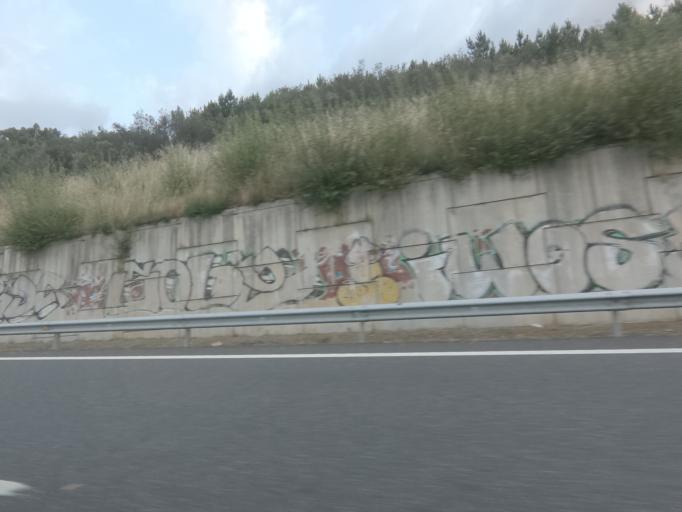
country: ES
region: Galicia
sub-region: Provincia de Ourense
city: Toen
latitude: 42.3360
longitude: -7.9851
